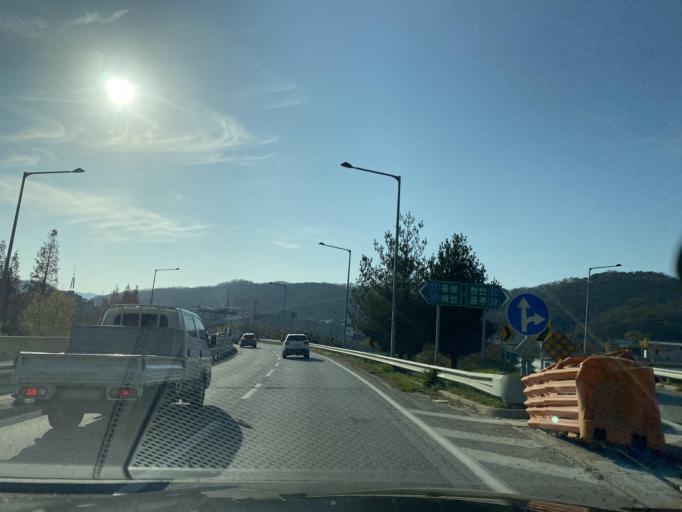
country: KR
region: Chungcheongnam-do
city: Asan
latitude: 36.7799
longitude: 126.9385
